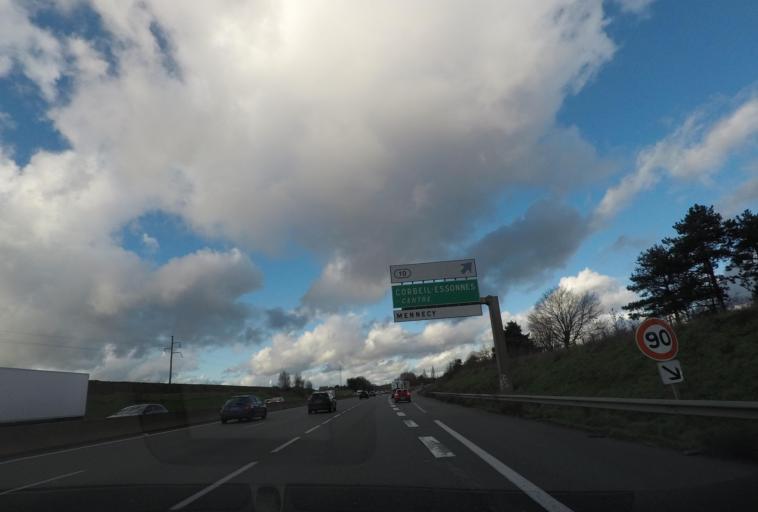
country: FR
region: Ile-de-France
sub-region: Departement de l'Essonne
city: Ormoy
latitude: 48.5686
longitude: 2.4715
